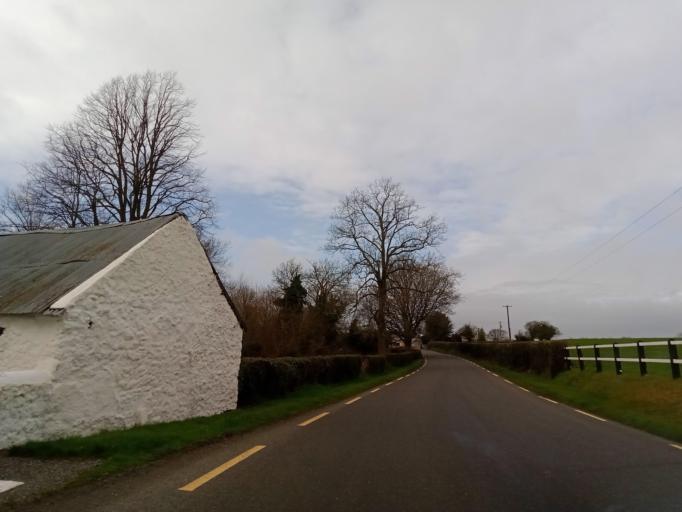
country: IE
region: Leinster
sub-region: Kilkenny
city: Ballyragget
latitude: 52.7191
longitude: -7.3123
